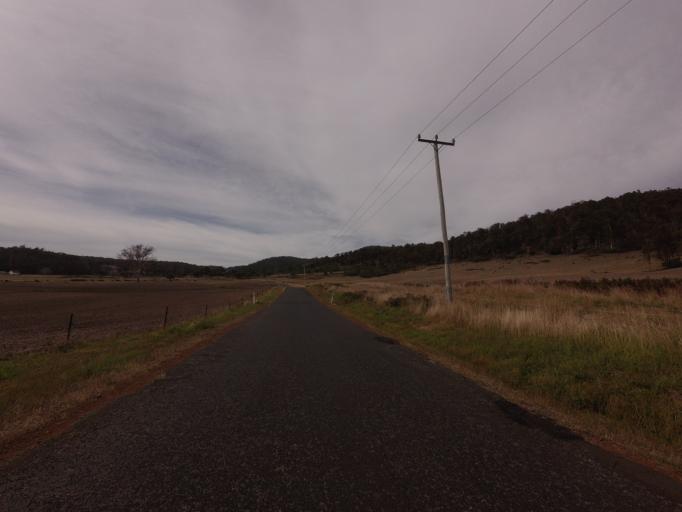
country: AU
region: Tasmania
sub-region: Sorell
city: Sorell
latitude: -42.4311
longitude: 147.5189
